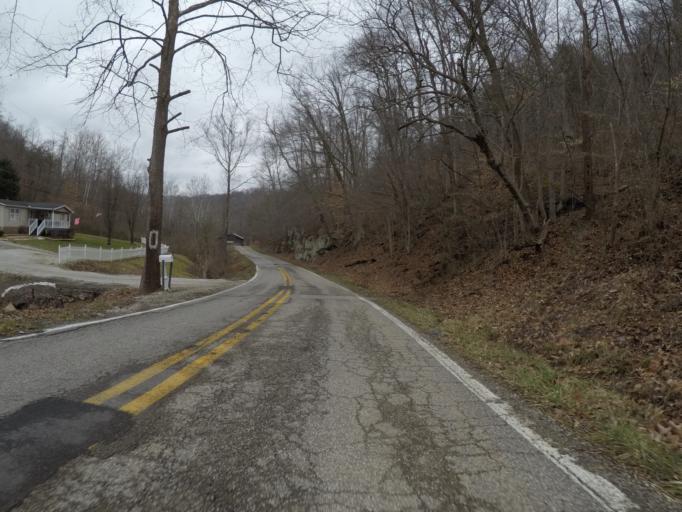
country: US
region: West Virginia
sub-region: Cabell County
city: Lesage
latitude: 38.4657
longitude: -82.2785
